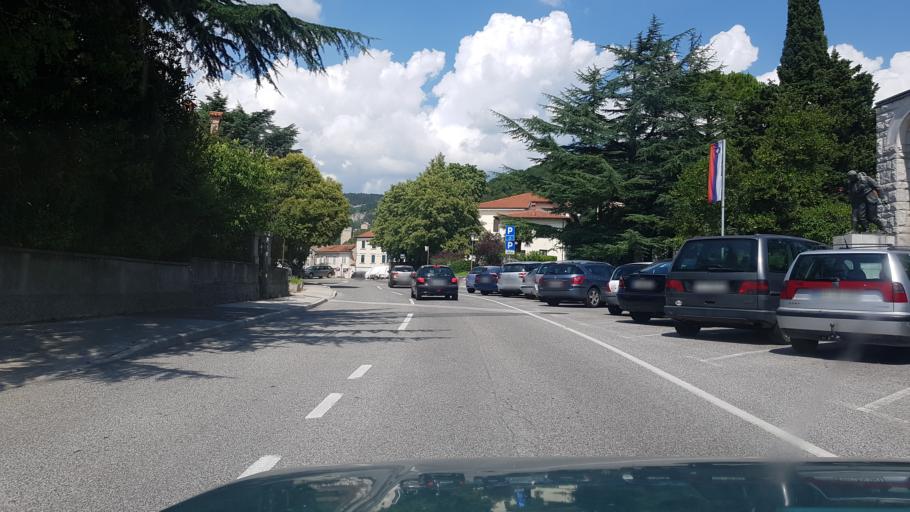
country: SI
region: Nova Gorica
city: Solkan
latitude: 45.9721
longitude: 13.6476
